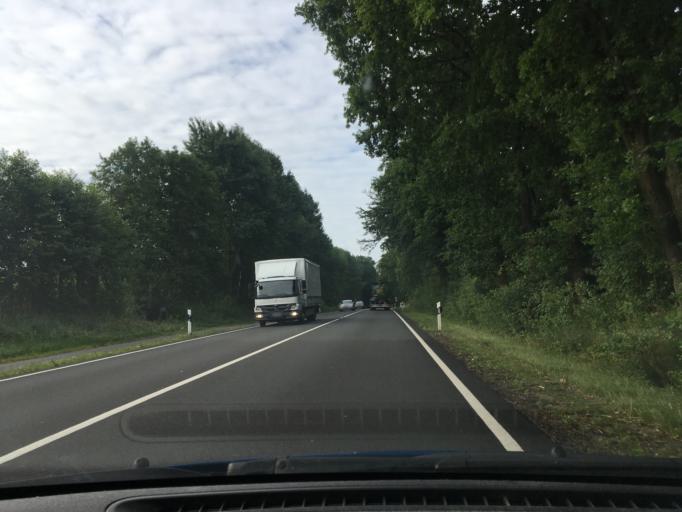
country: DE
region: Lower Saxony
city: Wenzendorf
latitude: 53.3671
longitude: 9.8055
